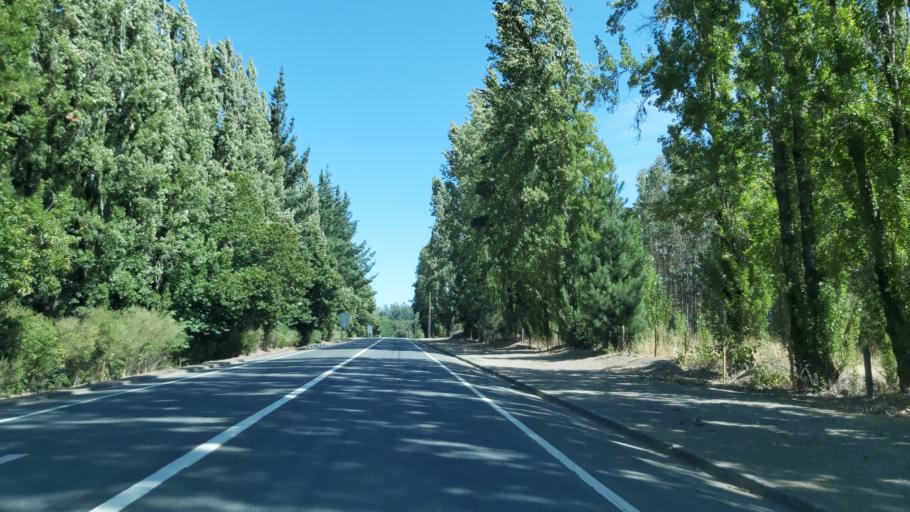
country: CL
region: Biobio
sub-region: Provincia de Concepcion
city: Coronel
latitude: -37.1062
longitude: -72.9890
